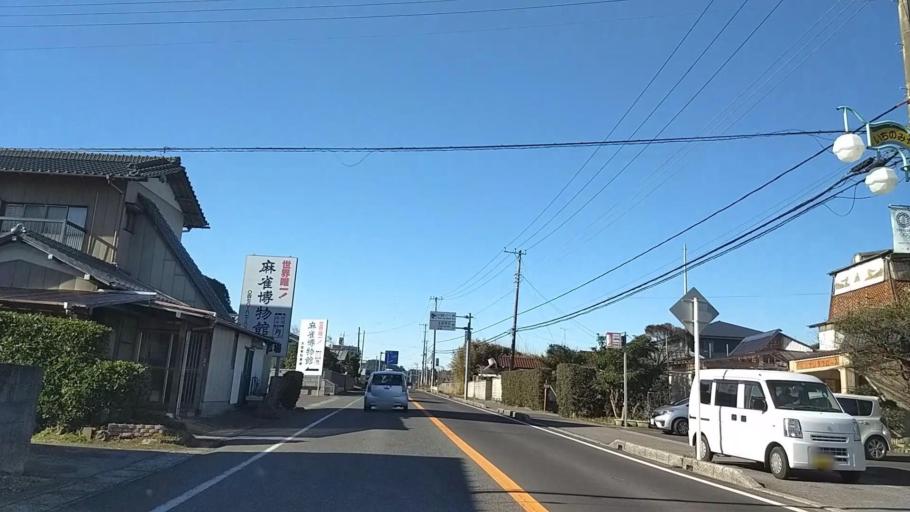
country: JP
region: Chiba
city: Ohara
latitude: 35.3316
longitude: 140.3947
